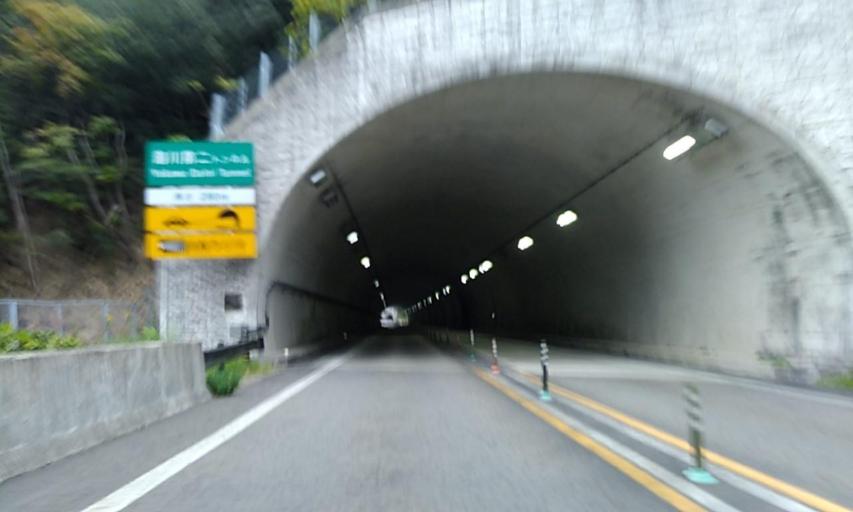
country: JP
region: Wakayama
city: Shingu
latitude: 33.6293
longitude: 135.9224
